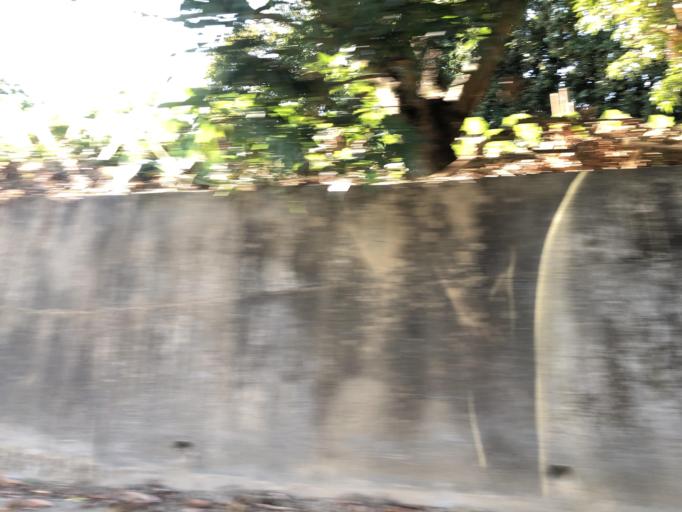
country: TW
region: Taiwan
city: Yujing
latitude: 23.0515
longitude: 120.4013
